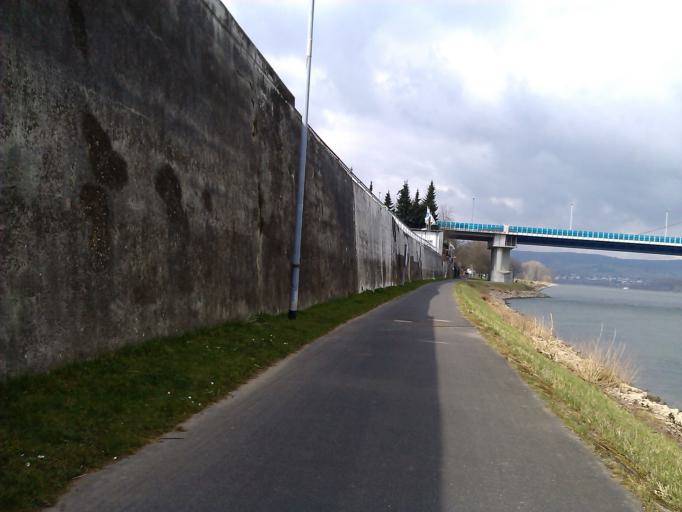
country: DE
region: Rheinland-Pfalz
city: Weissenthurm
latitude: 50.4181
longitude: 7.4567
